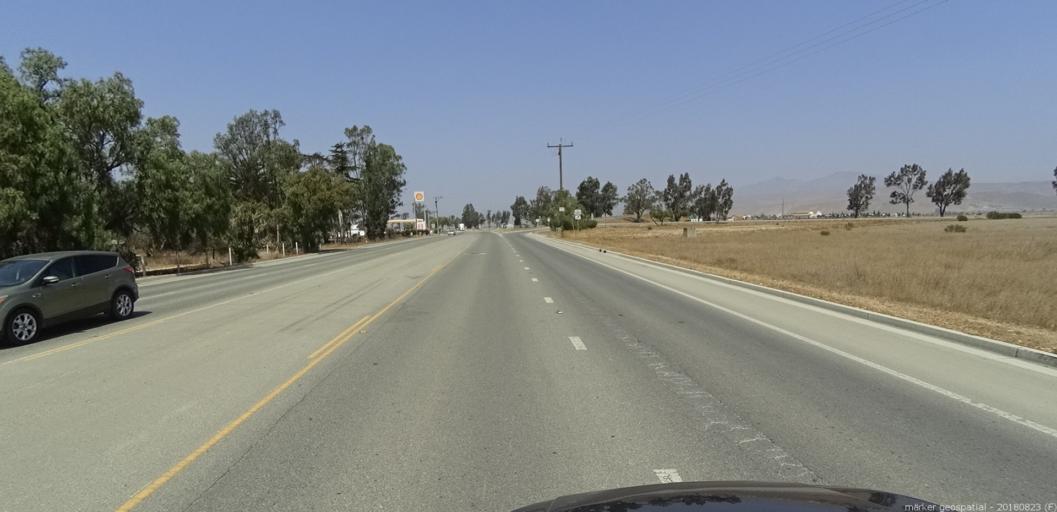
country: US
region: California
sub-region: Monterey County
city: Greenfield
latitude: 36.3368
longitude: -121.2556
